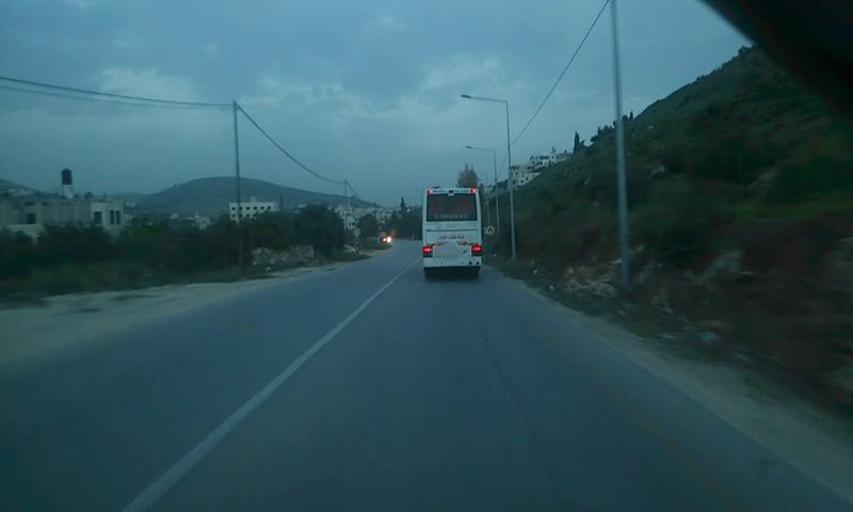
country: PS
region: West Bank
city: Kafr al Labad
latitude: 32.3107
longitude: 35.1052
